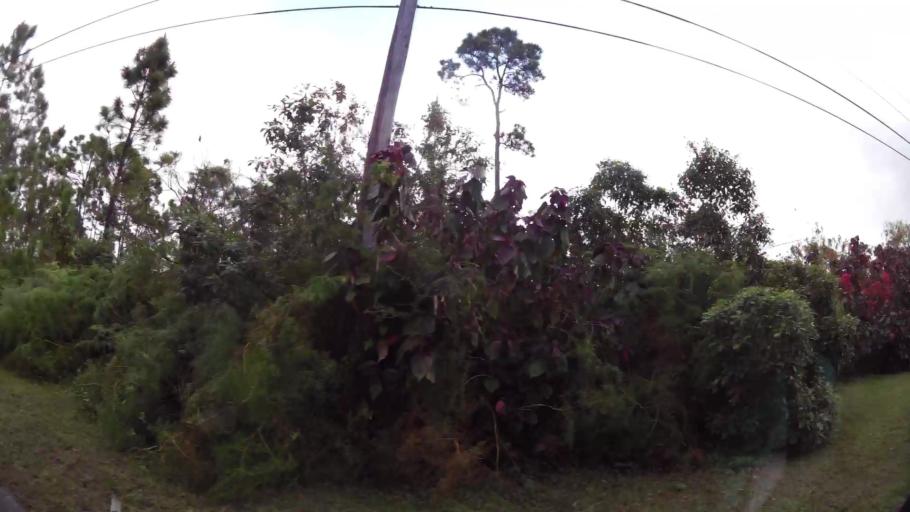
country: BS
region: Freeport
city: Lucaya
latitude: 26.5661
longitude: -78.5692
